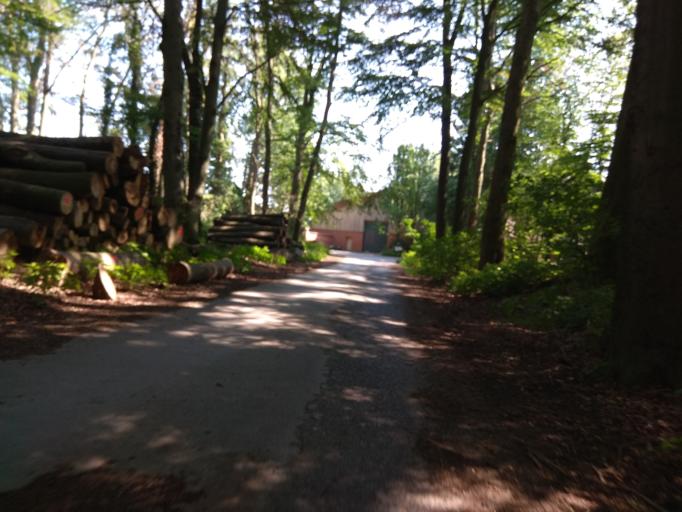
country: DE
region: North Rhine-Westphalia
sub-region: Regierungsbezirk Munster
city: Klein Reken
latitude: 51.7310
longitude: 7.0229
